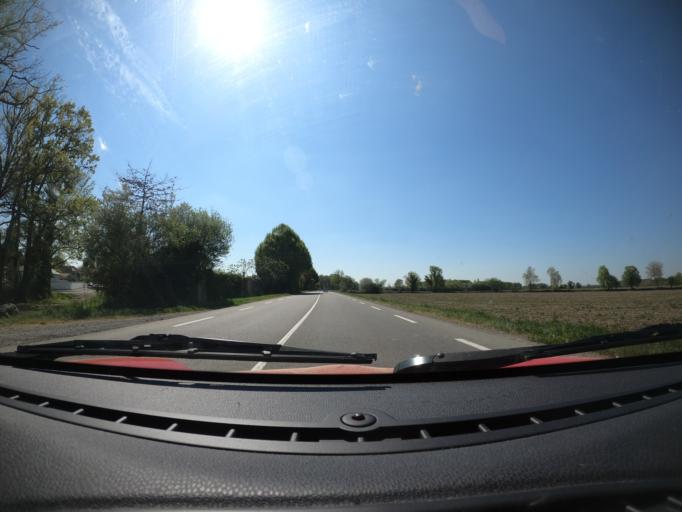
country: FR
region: Aquitaine
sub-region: Departement des Pyrenees-Atlantiques
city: Lons
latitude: 43.3405
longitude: -0.3922
